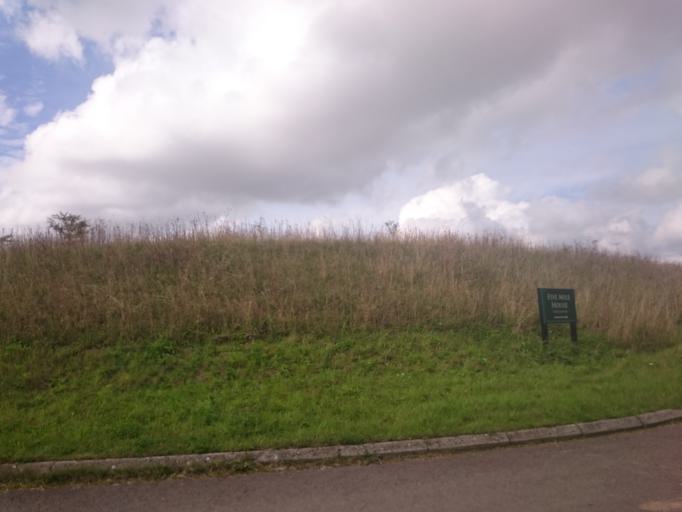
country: GB
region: England
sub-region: Gloucestershire
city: Coates
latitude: 51.7784
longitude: -2.0333
